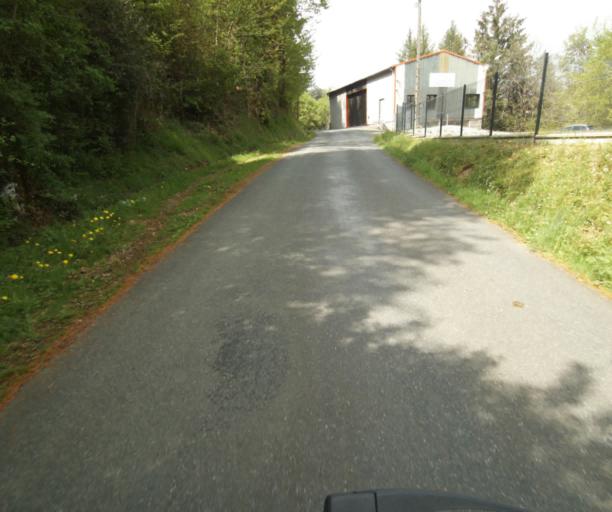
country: FR
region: Limousin
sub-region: Departement de la Correze
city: Tulle
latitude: 45.2752
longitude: 1.7610
